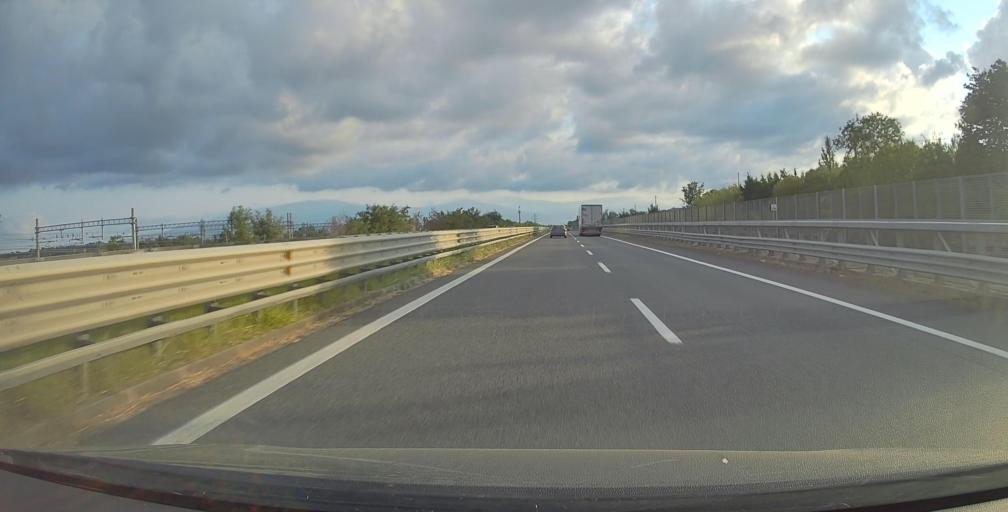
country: IT
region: Calabria
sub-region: Provincia di Catanzaro
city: Acconia
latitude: 38.8039
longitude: 16.2307
